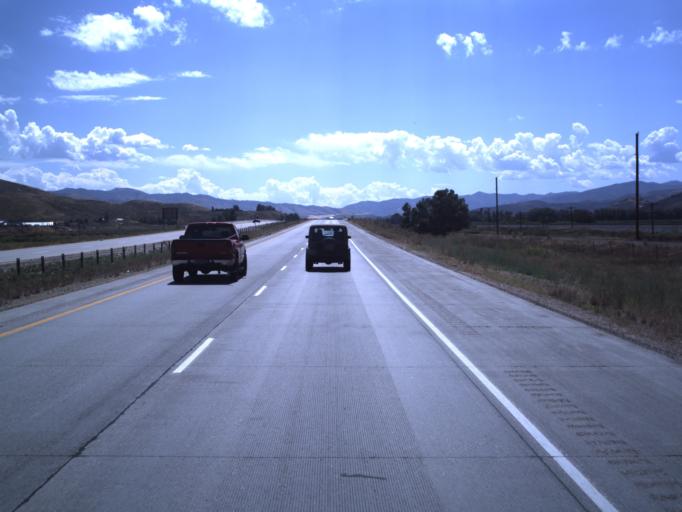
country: US
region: Utah
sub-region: Morgan County
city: Mountain Green
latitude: 41.1025
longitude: -111.7450
